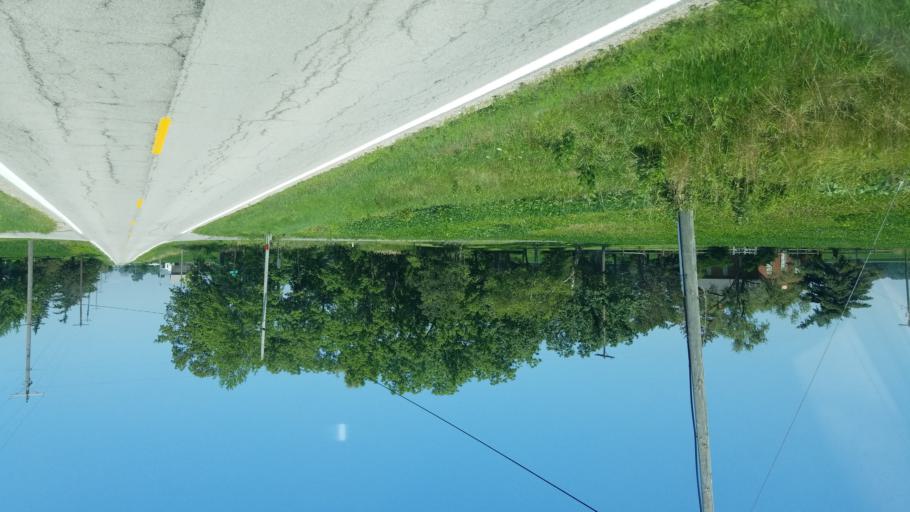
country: US
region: Ohio
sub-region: Sandusky County
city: Clyde
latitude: 41.3572
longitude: -82.9739
